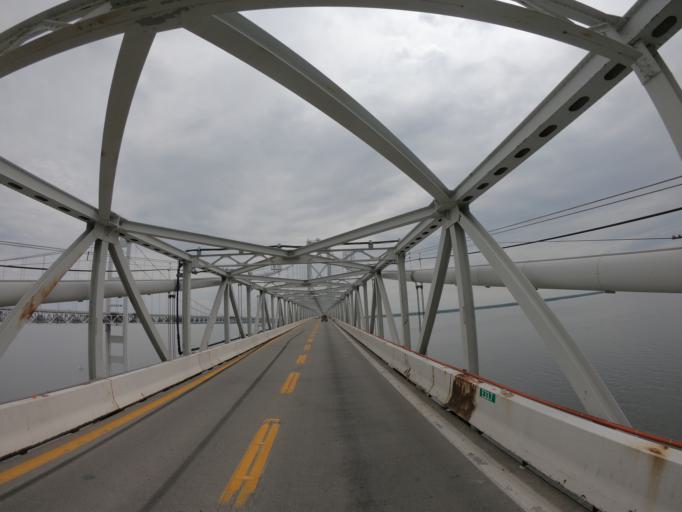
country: US
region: Maryland
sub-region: Queen Anne's County
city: Stevensville
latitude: 38.9943
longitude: -76.3868
